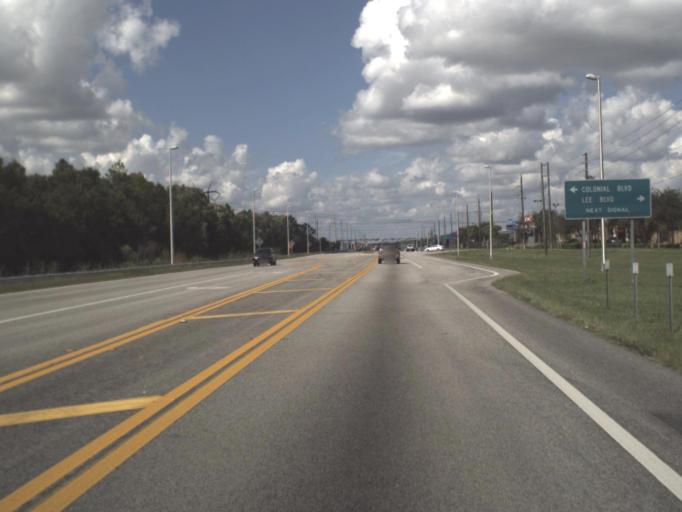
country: US
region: Florida
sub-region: Lee County
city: Gateway
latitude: 26.6147
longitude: -81.7632
